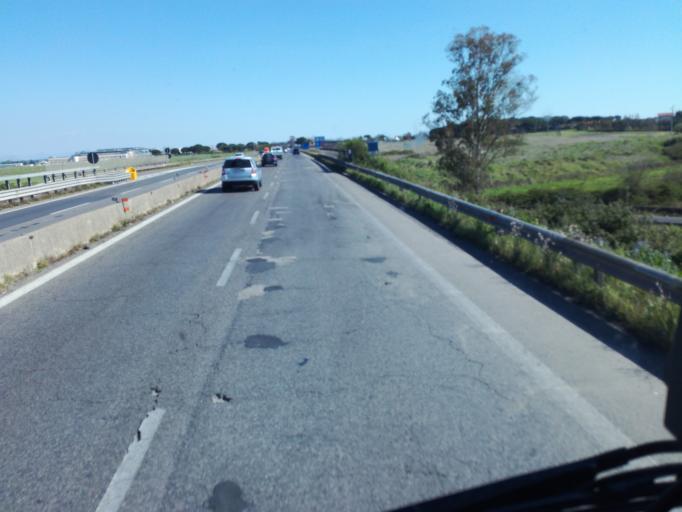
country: IT
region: Latium
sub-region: Provincia di Latina
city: Genio Civile
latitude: 41.5550
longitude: 12.6936
